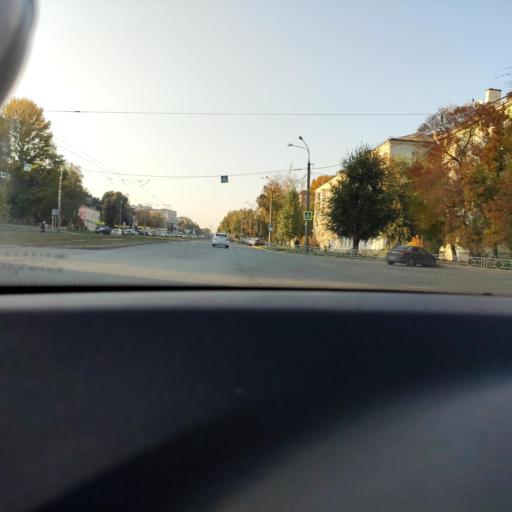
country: RU
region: Samara
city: Samara
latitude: 53.2093
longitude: 50.2319
